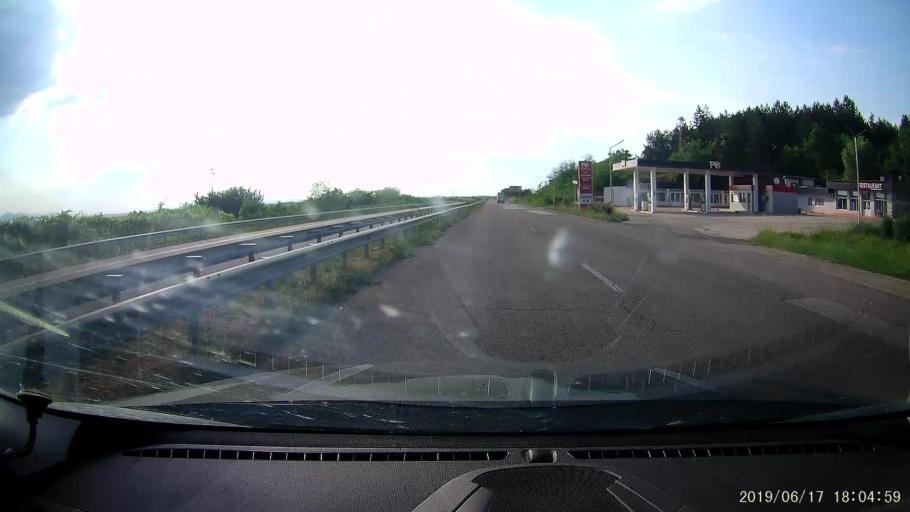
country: BG
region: Khaskovo
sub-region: Obshtina Svilengrad
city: Svilengrad
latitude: 41.7925
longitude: 26.1859
